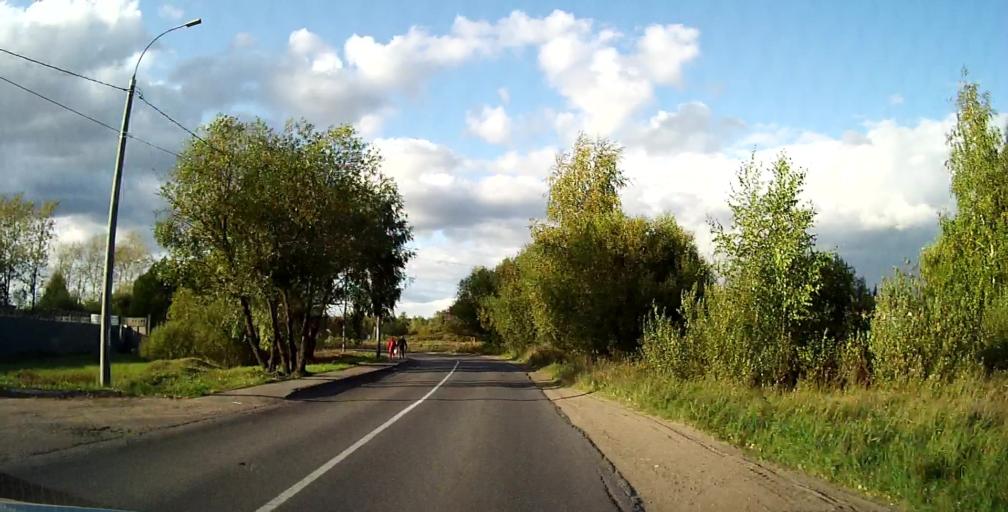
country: RU
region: Moskovskaya
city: Klimovsk
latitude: 55.3793
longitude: 37.5624
